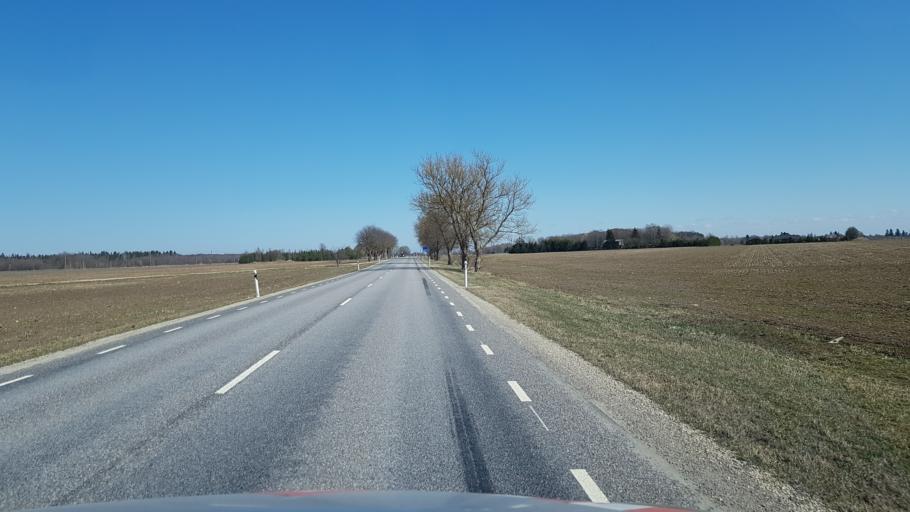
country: EE
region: Ida-Virumaa
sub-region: Johvi vald
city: Johvi
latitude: 59.3399
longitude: 27.3510
